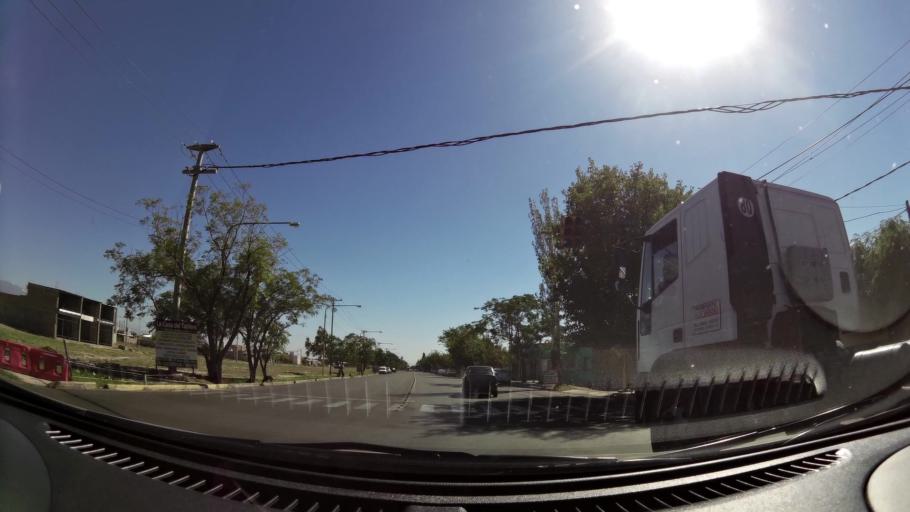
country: AR
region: Mendoza
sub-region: Departamento de Maipu
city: Maipu
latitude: -32.9699
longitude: -68.7927
